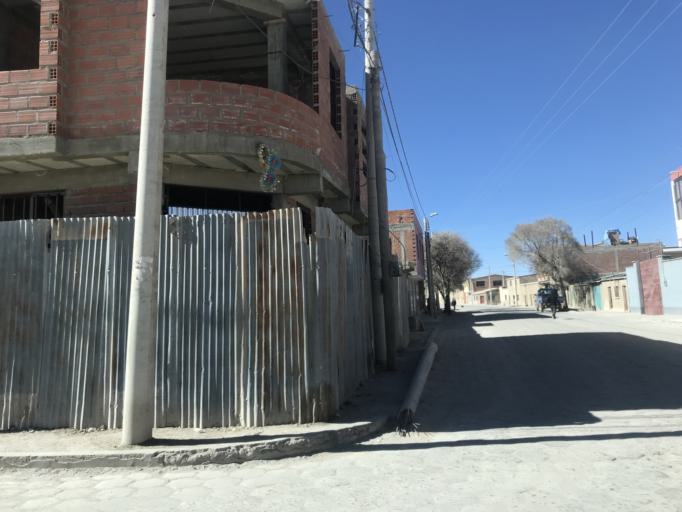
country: BO
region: Potosi
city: Uyuni
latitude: -20.4666
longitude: -66.8245
